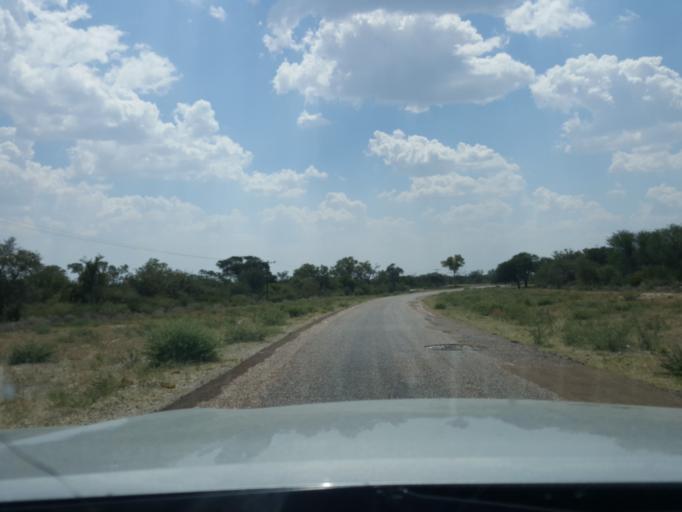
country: BW
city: Tsau
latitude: -19.9804
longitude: 22.2552
